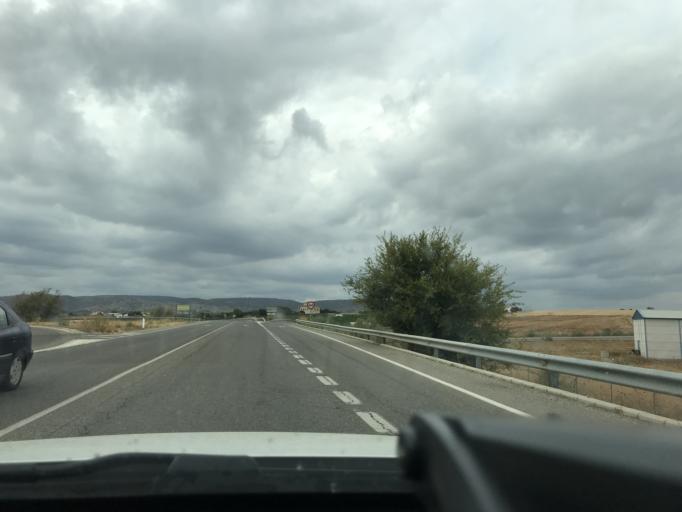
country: ES
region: Andalusia
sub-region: Provincia de Sevilla
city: Cantillana
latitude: 37.6186
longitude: -5.8144
